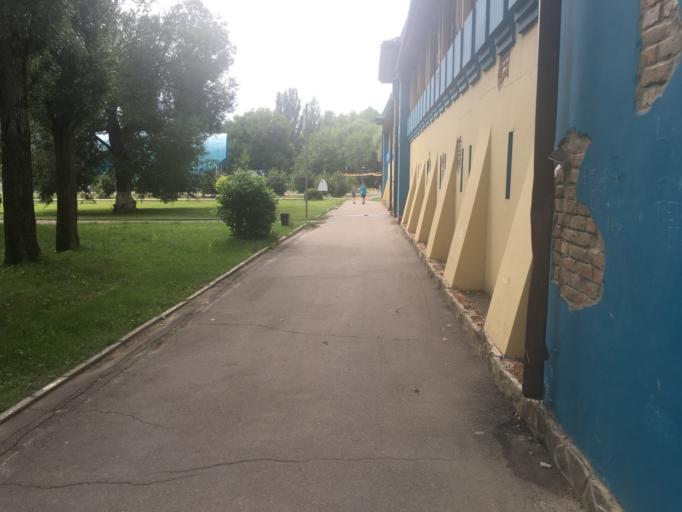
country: RU
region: Voronezj
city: Rossosh'
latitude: 50.1956
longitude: 39.5778
